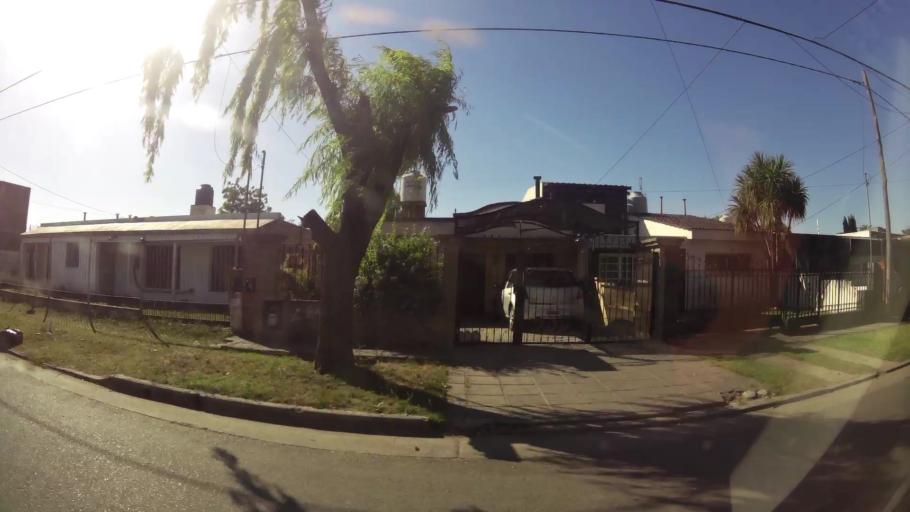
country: AR
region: Cordoba
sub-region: Departamento de Capital
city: Cordoba
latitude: -31.3628
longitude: -64.1882
